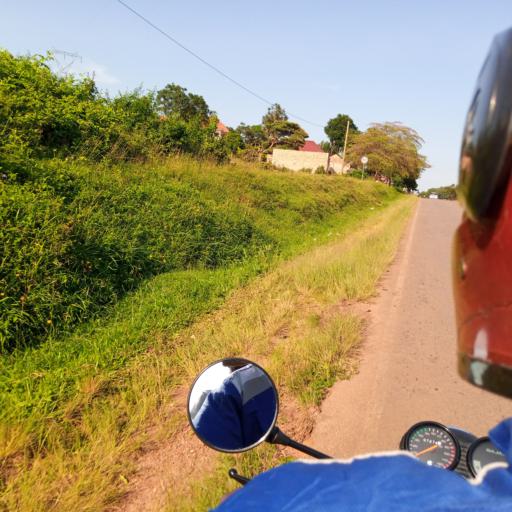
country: UG
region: Central Region
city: Masaka
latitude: -0.4167
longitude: 31.6769
